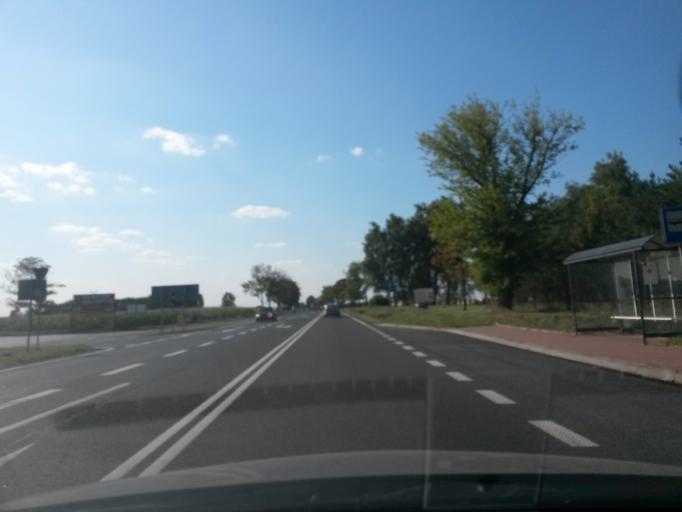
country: PL
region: Masovian Voivodeship
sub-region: Powiat sierpecki
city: Zawidz
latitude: 52.7986
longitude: 19.8607
